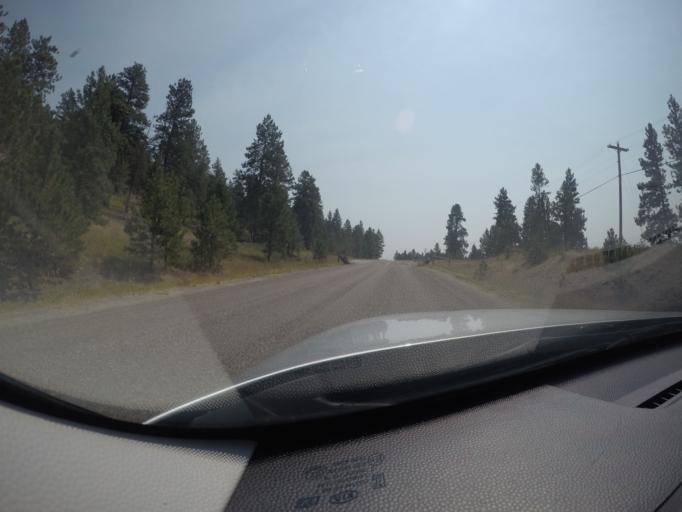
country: US
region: Montana
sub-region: Lake County
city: Polson
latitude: 47.7661
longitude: -114.1669
